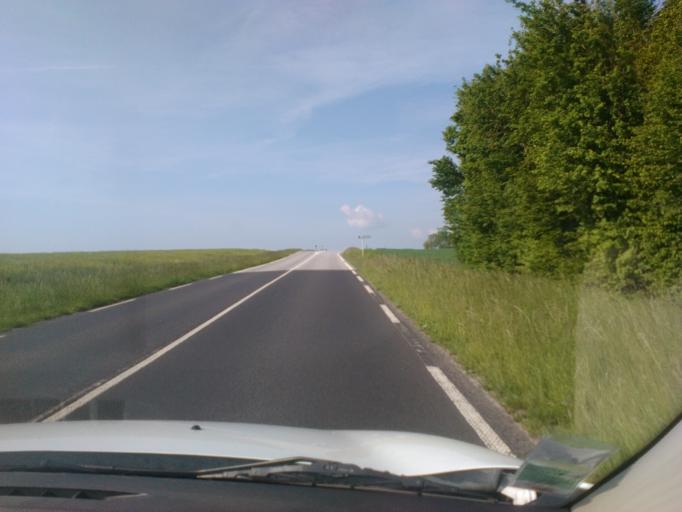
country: FR
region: Lorraine
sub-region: Departement des Vosges
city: Mirecourt
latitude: 48.3348
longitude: 6.1396
